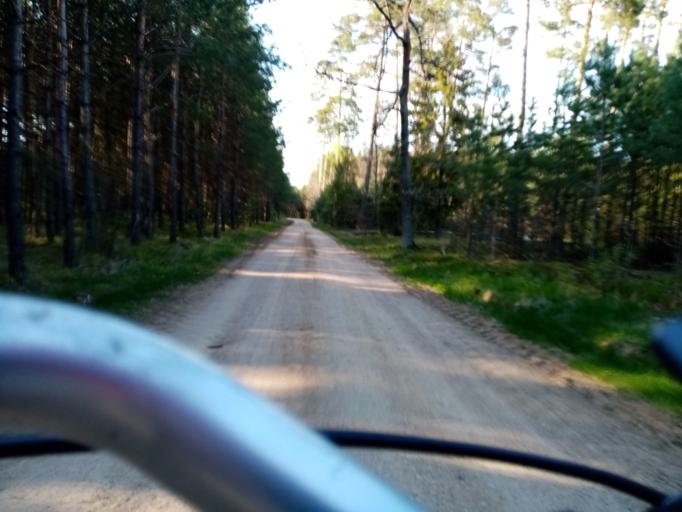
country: PL
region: Kujawsko-Pomorskie
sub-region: Powiat brodnicki
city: Gorzno
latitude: 53.1556
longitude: 19.7011
